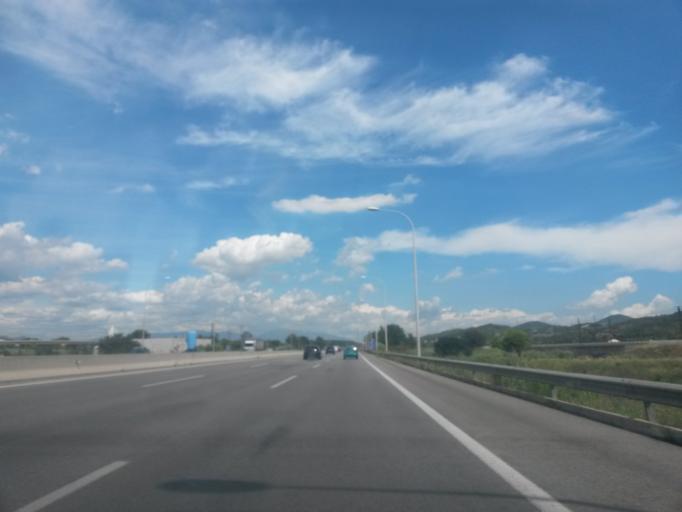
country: ES
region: Catalonia
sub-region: Provincia de Barcelona
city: La Llagosta
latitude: 41.5019
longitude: 2.1960
